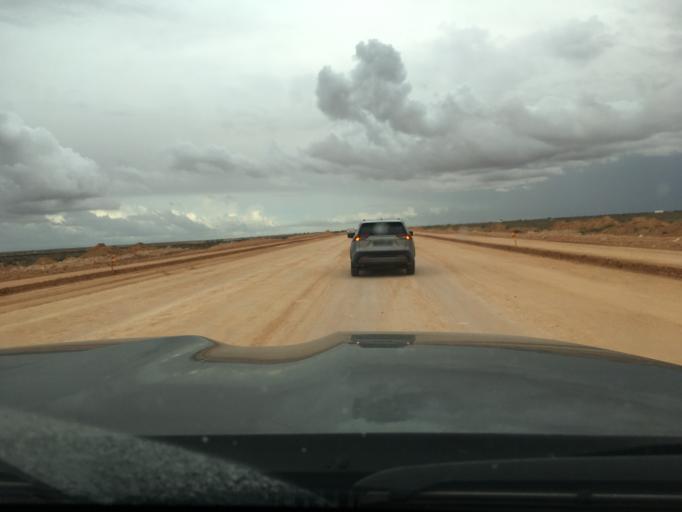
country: TN
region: Madanin
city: Medenine
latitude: 33.2788
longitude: 10.5936
